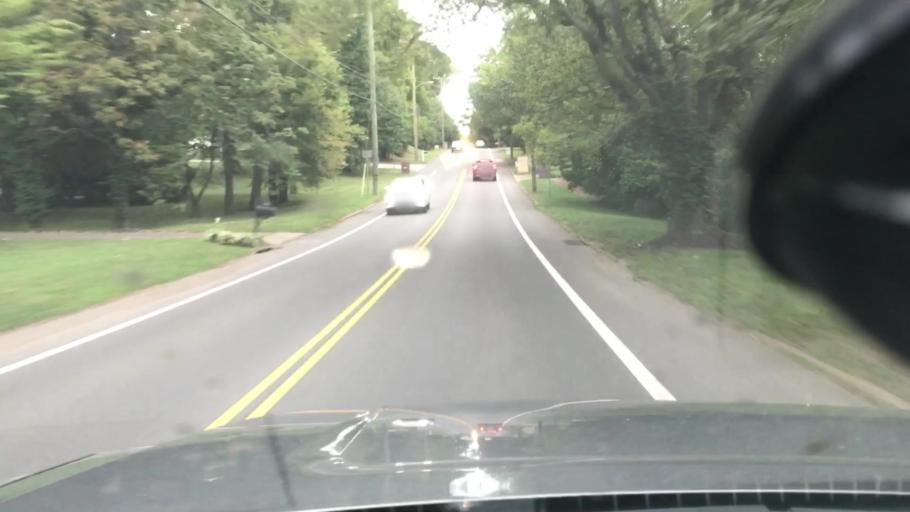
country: US
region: Tennessee
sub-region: Davidson County
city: Oak Hill
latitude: 36.1146
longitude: -86.8171
